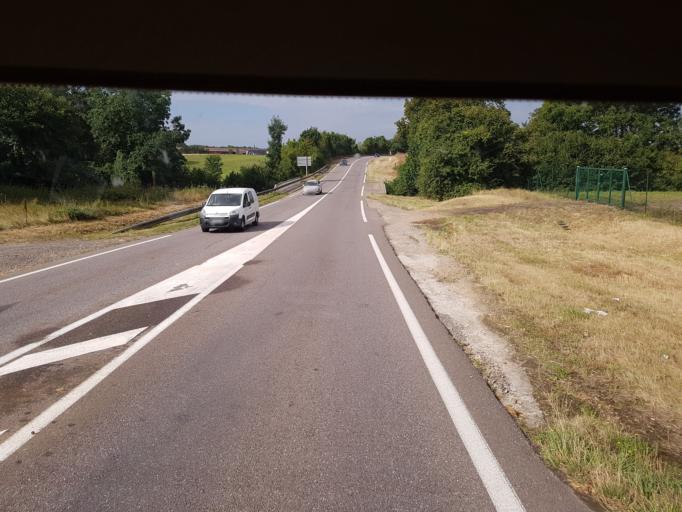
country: FR
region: Lorraine
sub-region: Departement de la Moselle
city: Koenigsmacker
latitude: 49.4073
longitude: 6.3045
